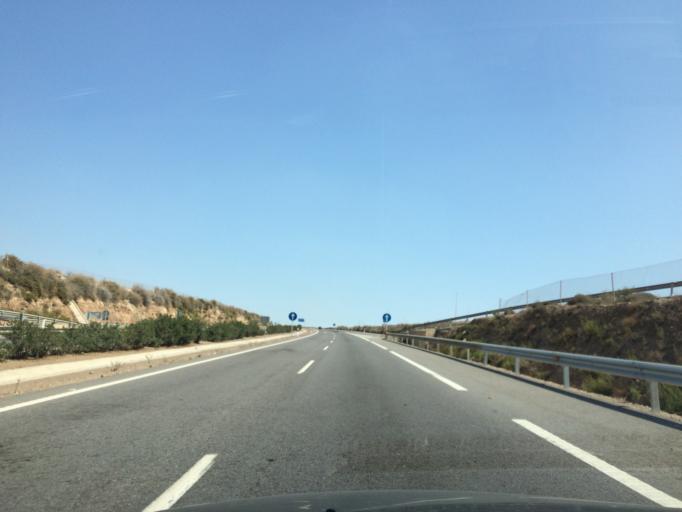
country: ES
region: Andalusia
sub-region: Provincia de Almeria
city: Dalias
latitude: 36.7568
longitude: -2.9162
